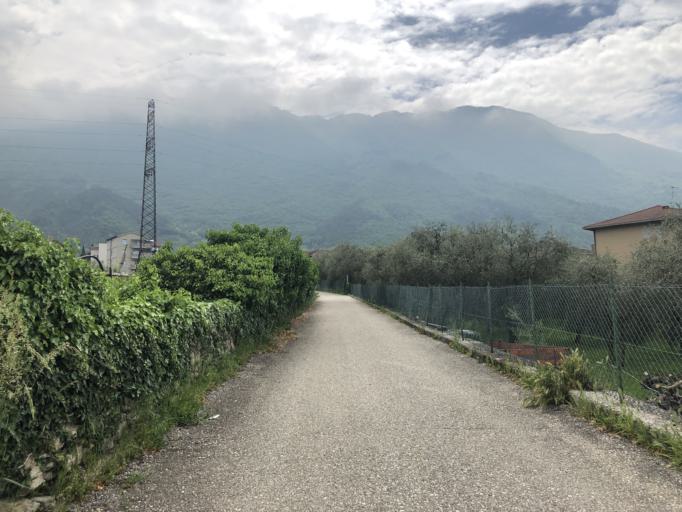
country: IT
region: Trentino-Alto Adige
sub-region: Provincia di Trento
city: Bolognano-Vignole
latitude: 45.9139
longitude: 10.8994
